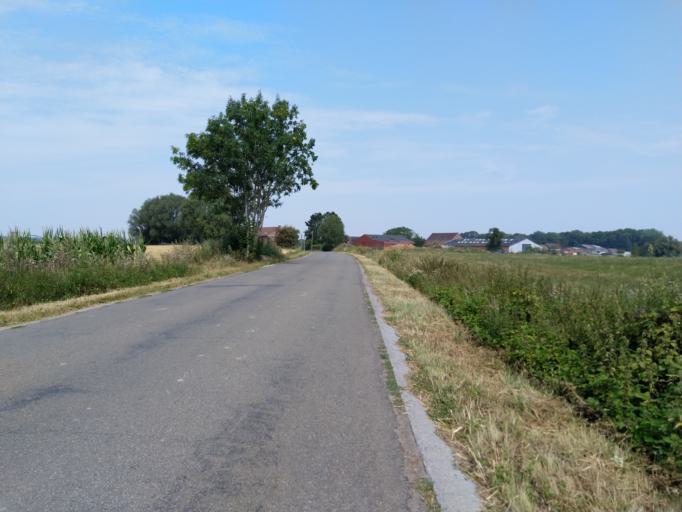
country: BE
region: Wallonia
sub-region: Province du Hainaut
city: Roeulx
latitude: 50.5049
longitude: 4.0506
